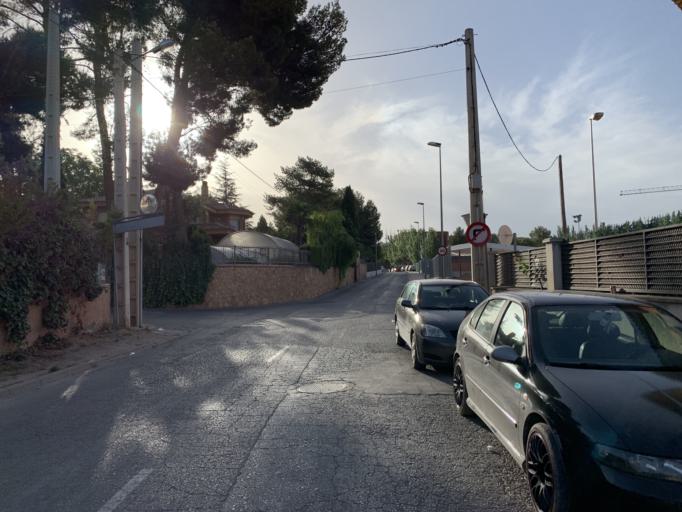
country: ES
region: Aragon
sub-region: Provincia de Teruel
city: Teruel
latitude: 40.3538
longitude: -1.1130
